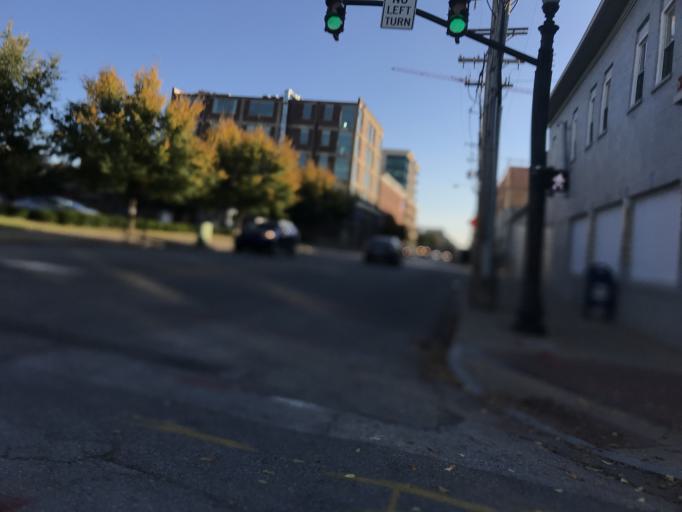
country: US
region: Kentucky
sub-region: Jefferson County
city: Louisville
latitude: 38.2555
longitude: -85.7480
